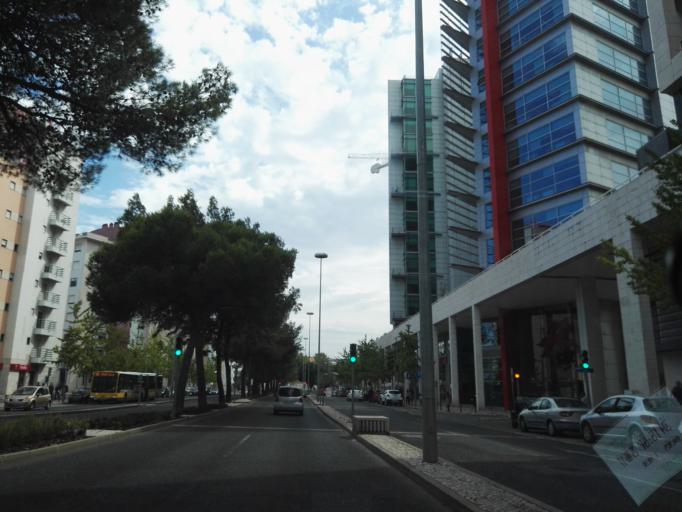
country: PT
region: Lisbon
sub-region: Loures
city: Moscavide
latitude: 38.7648
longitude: -9.0983
